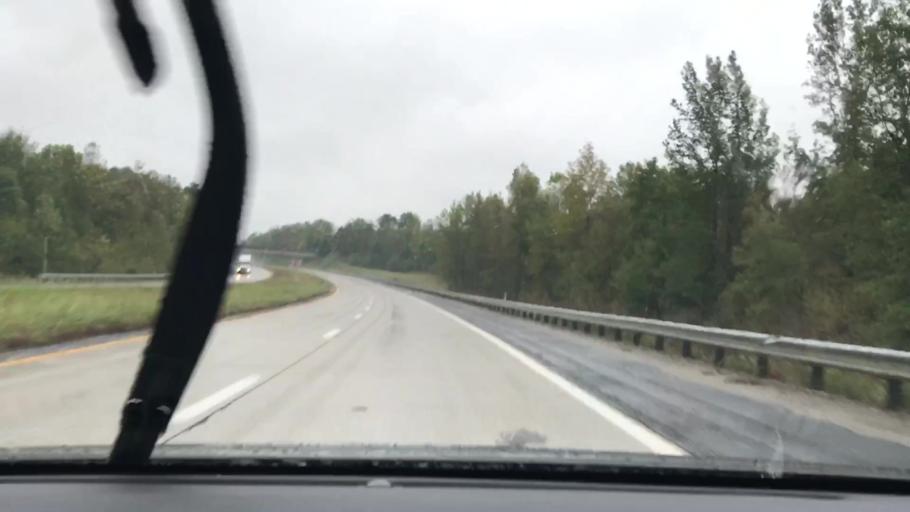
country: US
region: Kentucky
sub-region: Hopkins County
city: Nortonville
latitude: 37.1457
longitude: -87.4651
